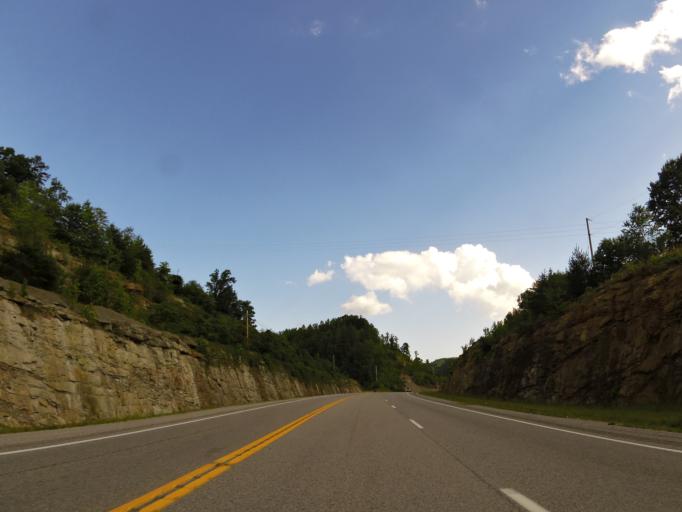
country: US
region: Kentucky
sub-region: Harlan County
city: Harlan
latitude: 36.8120
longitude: -83.2699
